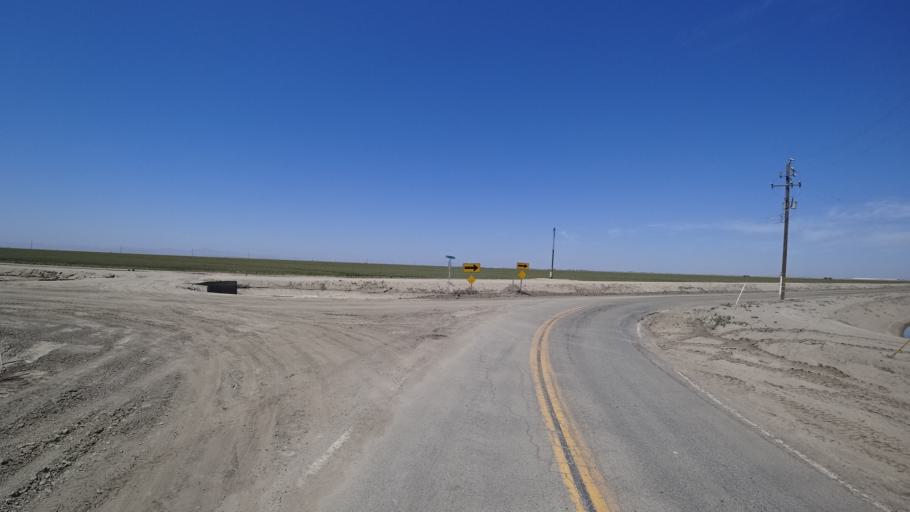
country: US
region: California
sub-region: Kings County
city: Corcoran
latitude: 36.1169
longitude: -119.6800
